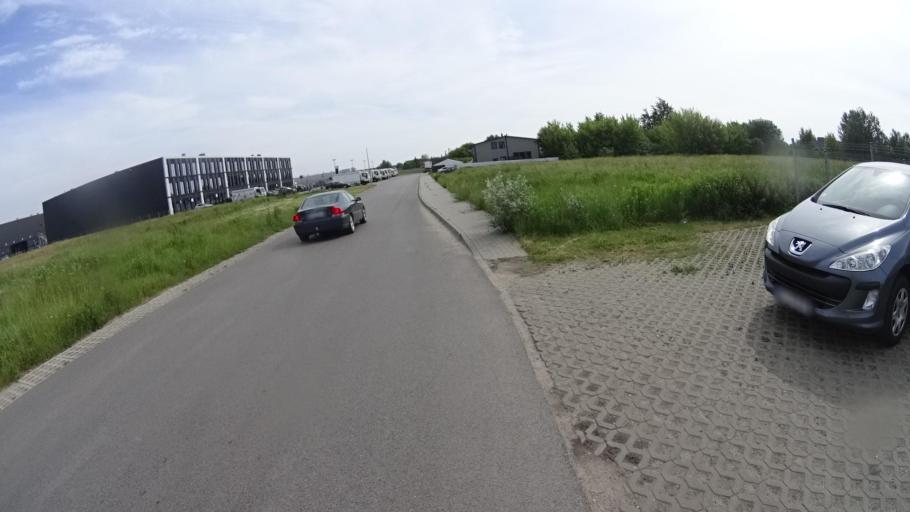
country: PL
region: Masovian Voivodeship
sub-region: Warszawa
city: Wlochy
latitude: 52.1868
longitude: 20.9333
